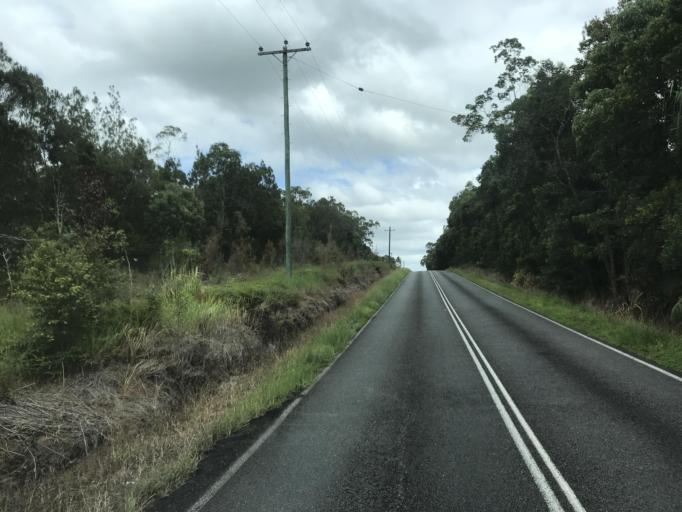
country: AU
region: Queensland
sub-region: Cassowary Coast
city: Innisfail
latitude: -17.8441
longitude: 146.0562
